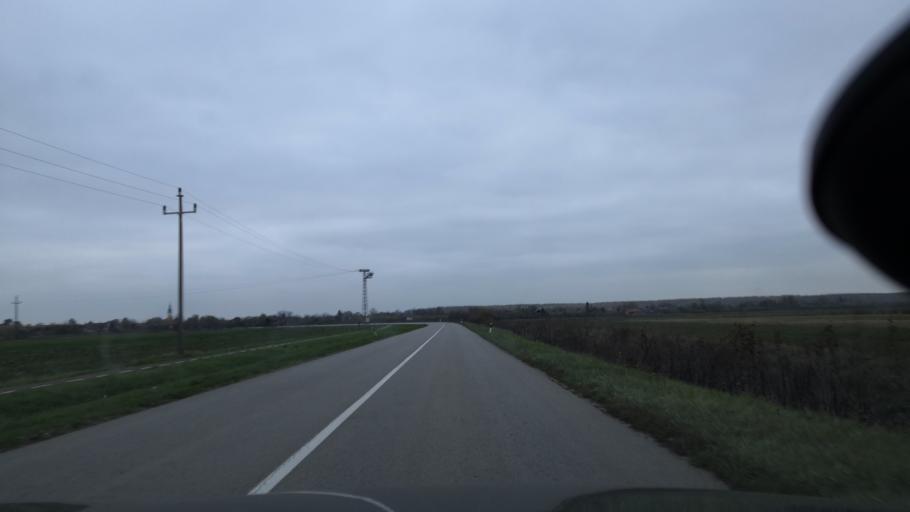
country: HU
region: Csongrad
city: Roszke
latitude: 46.1352
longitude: 20.0936
